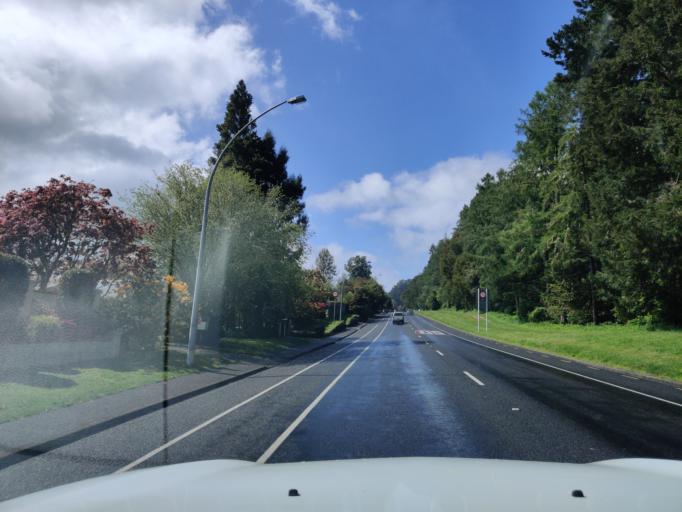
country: NZ
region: Bay of Plenty
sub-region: Rotorua District
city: Rotorua
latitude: -38.1513
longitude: 176.2831
